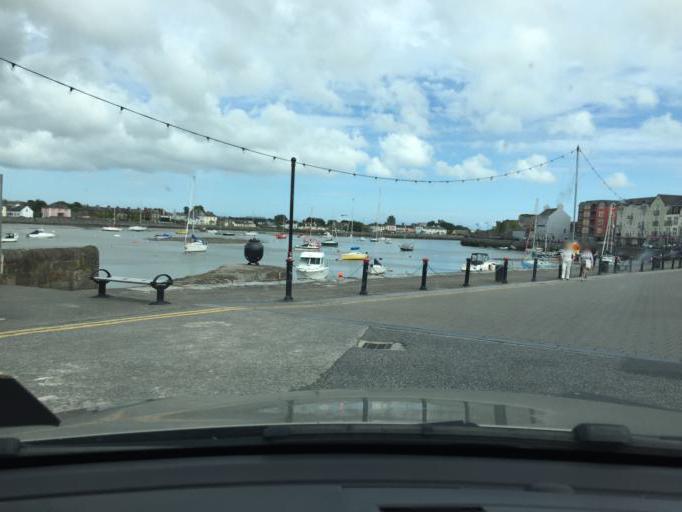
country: IE
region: Munster
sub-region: Waterford
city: Dungarvan
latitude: 52.0910
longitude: -7.6200
